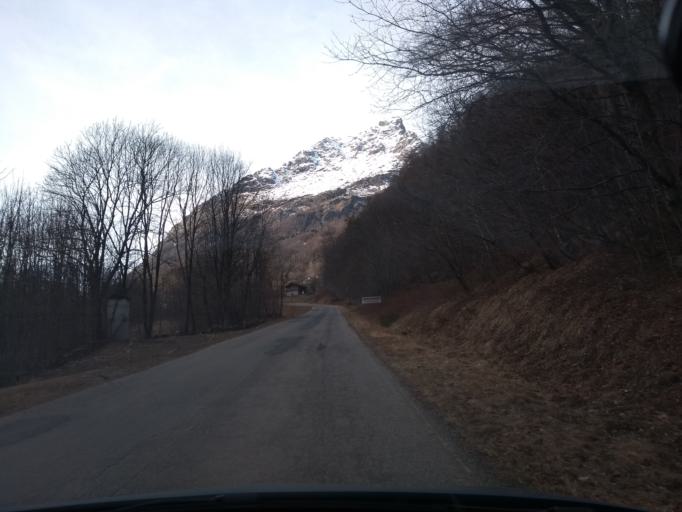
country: IT
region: Piedmont
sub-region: Provincia di Torino
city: Ala di Stura
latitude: 45.3123
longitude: 7.2652
